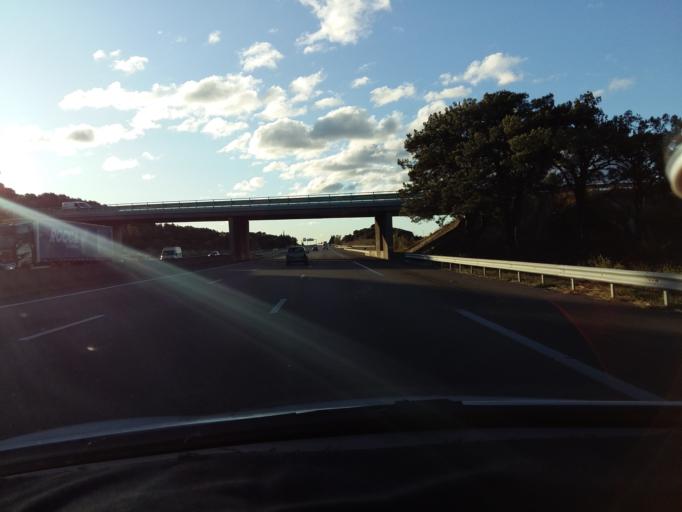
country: FR
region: Provence-Alpes-Cote d'Azur
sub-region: Departement du Vaucluse
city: Vedene
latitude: 43.9813
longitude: 4.8926
